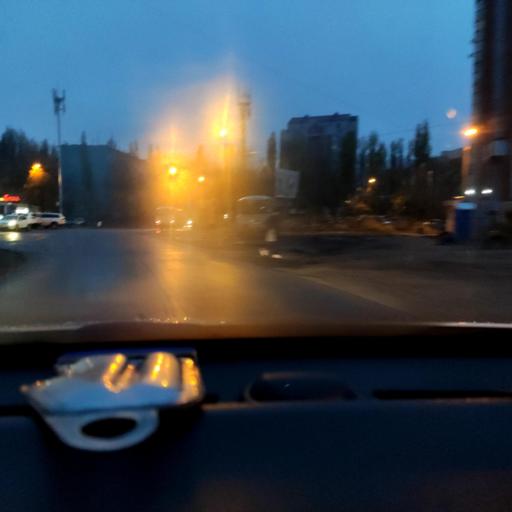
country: RU
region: Voronezj
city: Voronezh
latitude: 51.6956
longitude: 39.2639
